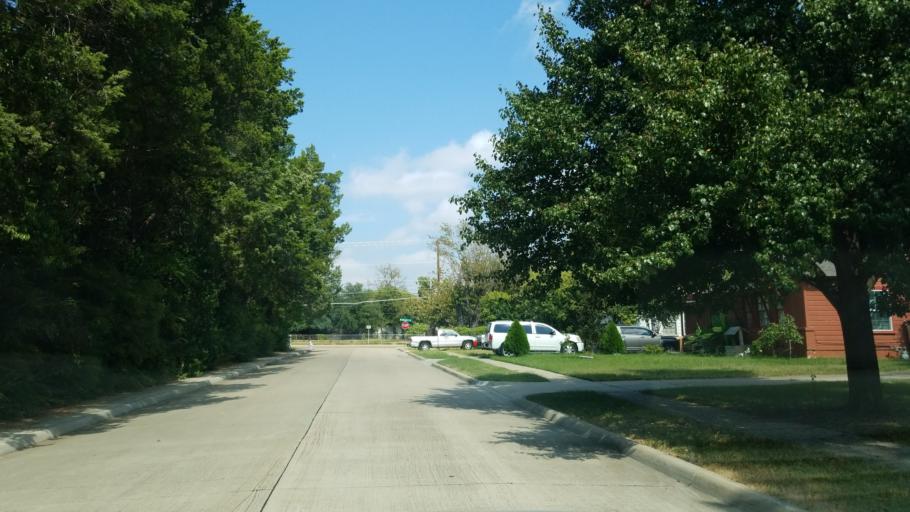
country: US
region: Texas
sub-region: Dallas County
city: Garland
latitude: 32.8938
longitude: -96.6556
